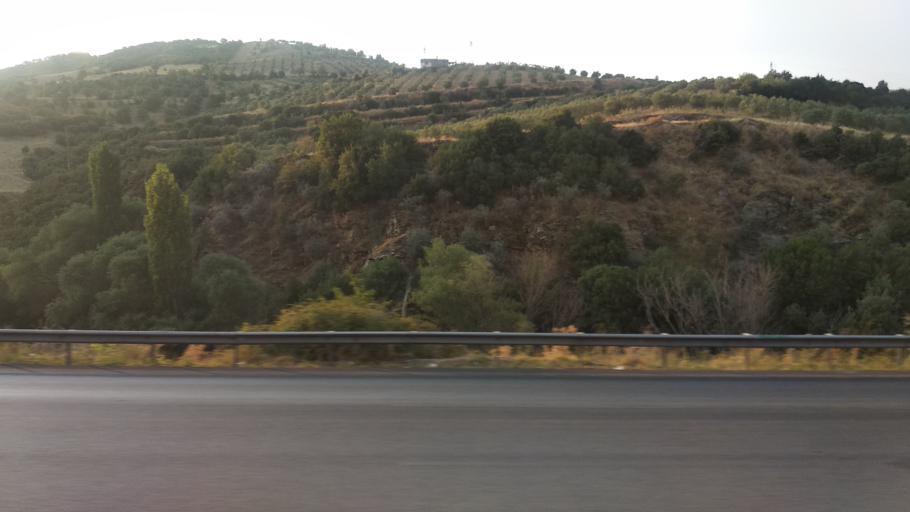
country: TR
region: Manisa
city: Menye
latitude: 38.5470
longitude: 28.4537
